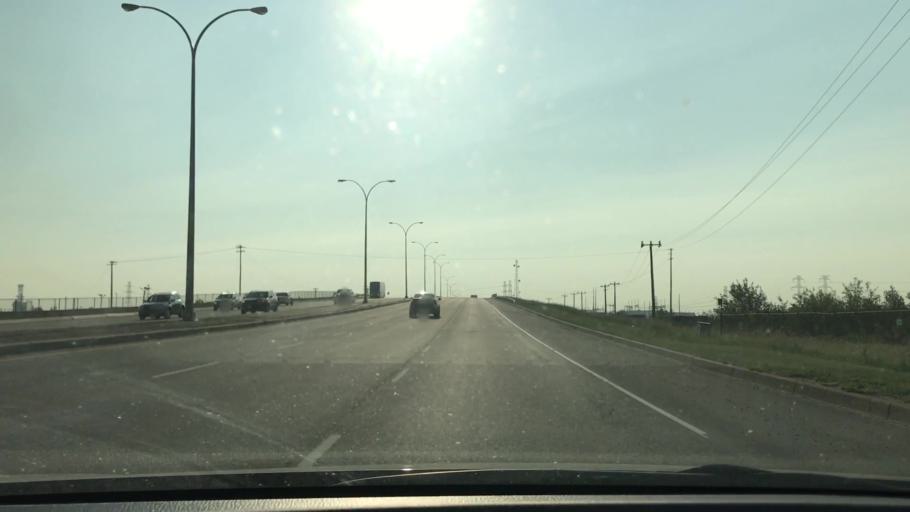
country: CA
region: Alberta
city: Sherwood Park
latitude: 53.5404
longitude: -113.3848
